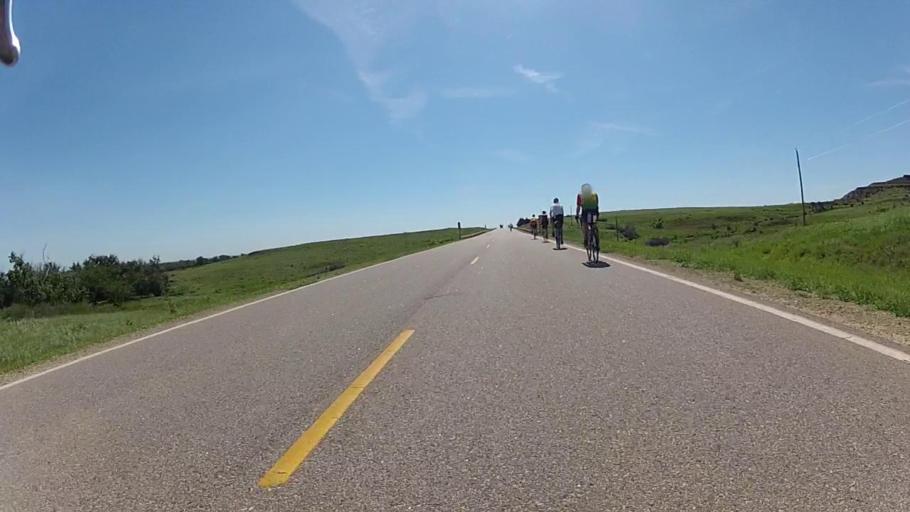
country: US
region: Kansas
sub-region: Barber County
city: Medicine Lodge
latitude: 37.2754
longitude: -98.7112
